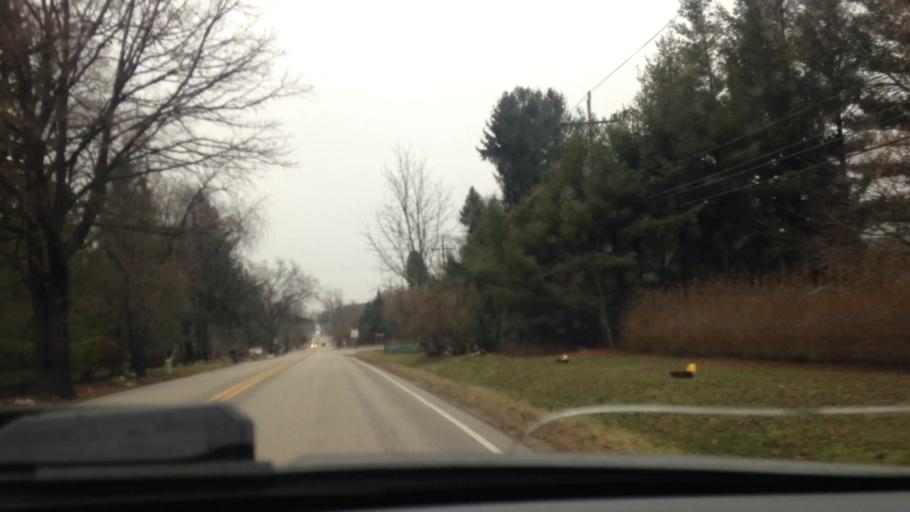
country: US
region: Wisconsin
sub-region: Waukesha County
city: Lannon
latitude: 43.1693
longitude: -88.1832
